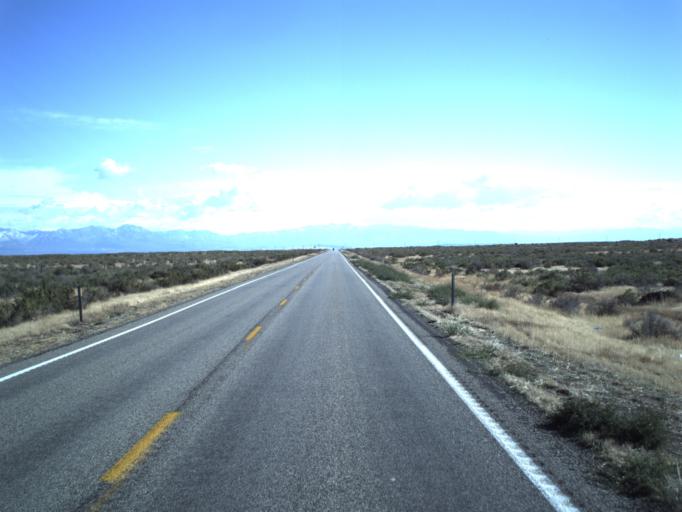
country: US
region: Utah
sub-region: Millard County
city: Delta
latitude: 39.3170
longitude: -112.4801
